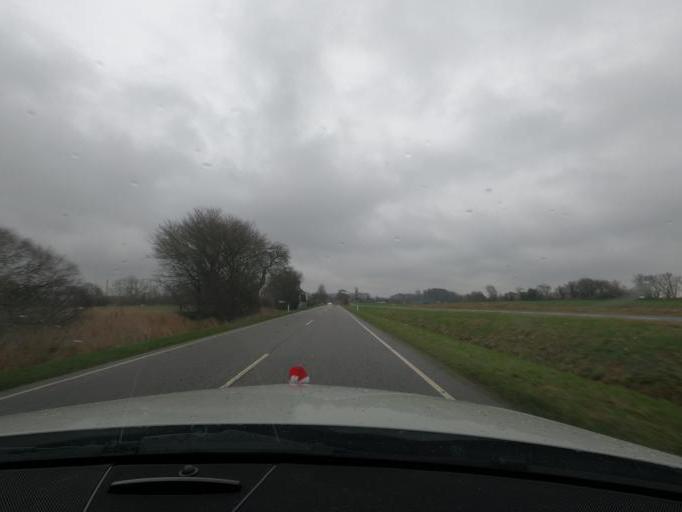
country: DK
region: South Denmark
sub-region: Haderslev Kommune
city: Starup
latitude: 55.2539
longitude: 9.6302
